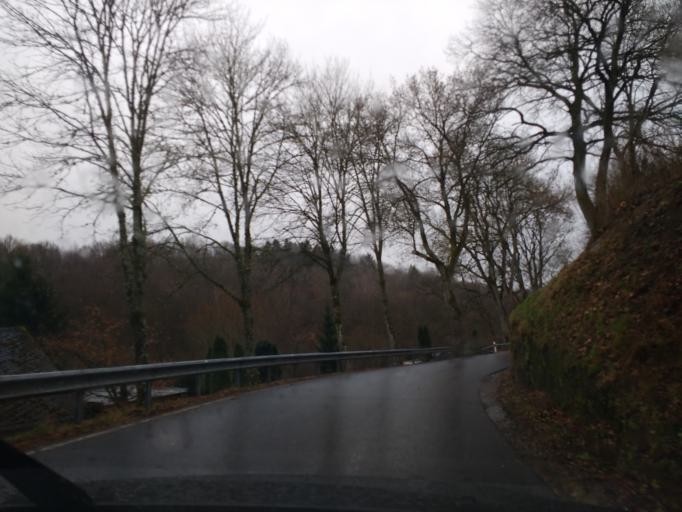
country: DE
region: Rheinland-Pfalz
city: Thalfang
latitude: 49.7489
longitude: 6.9997
